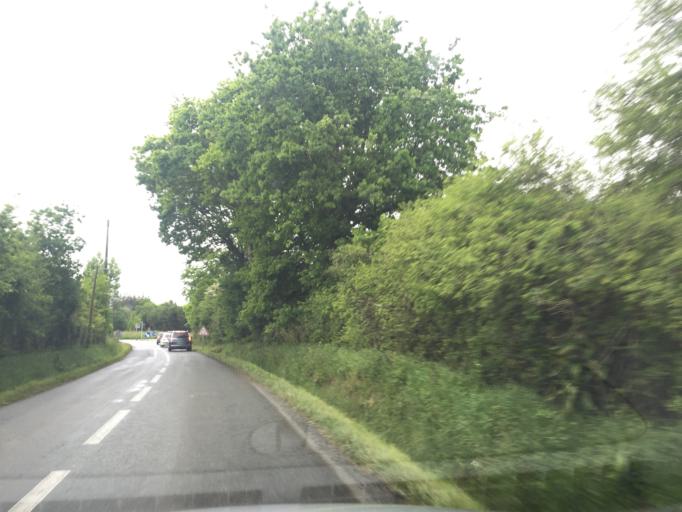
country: FR
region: Brittany
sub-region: Departement d'Ille-et-Vilaine
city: Saint-Lunaire
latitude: 48.6130
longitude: -2.1019
